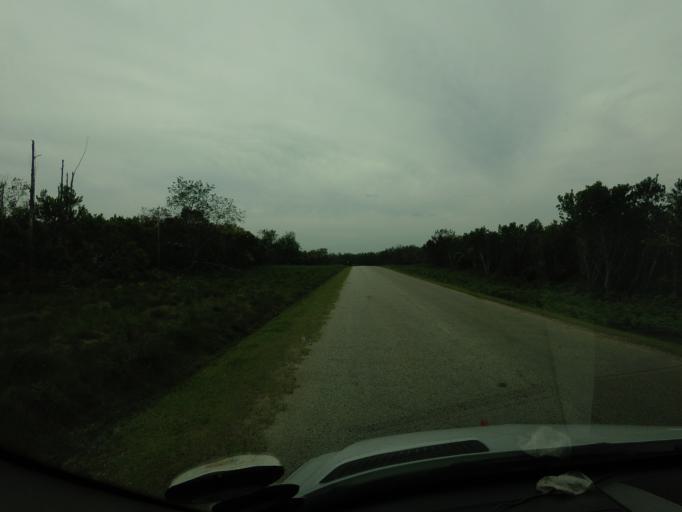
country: ZA
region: Eastern Cape
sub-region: Cacadu District Municipality
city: Kareedouw
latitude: -33.9681
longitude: 23.8873
